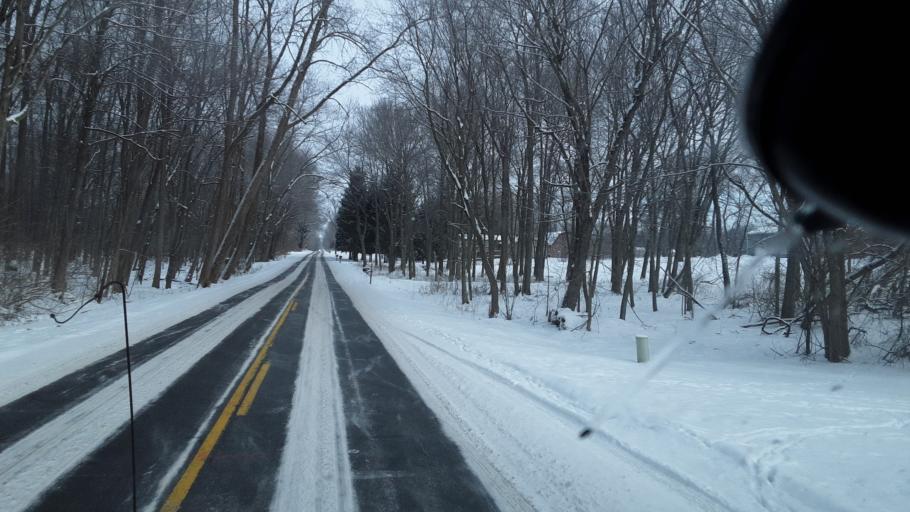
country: US
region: Michigan
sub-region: Jackson County
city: Jackson
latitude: 42.3118
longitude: -84.4829
